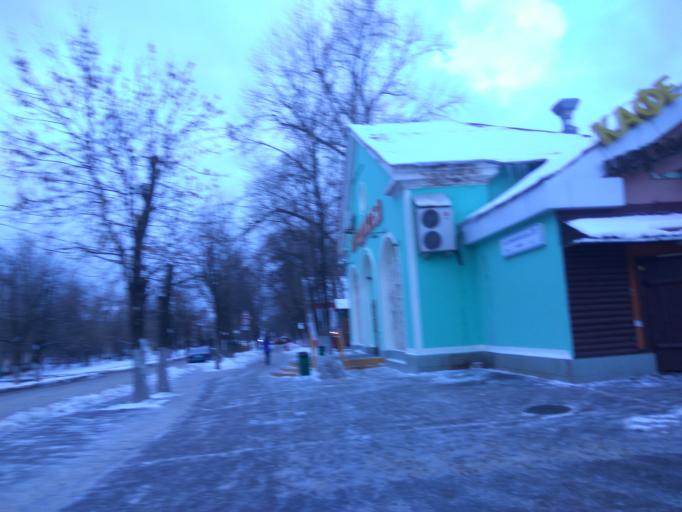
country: RU
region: Moskovskaya
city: Kur'yanovo
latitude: 55.6548
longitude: 37.7032
